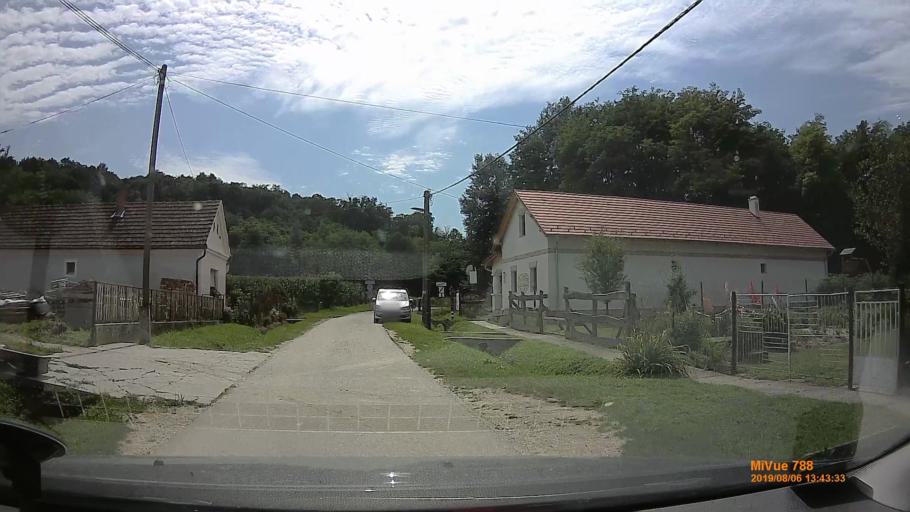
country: HU
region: Zala
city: Zalakomar
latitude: 46.5703
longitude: 17.0938
